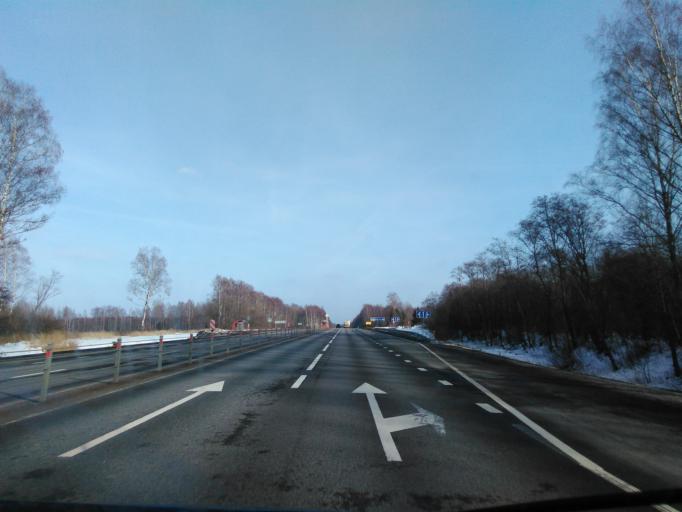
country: RU
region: Smolensk
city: Vyaz'ma
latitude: 55.1885
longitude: 34.0340
